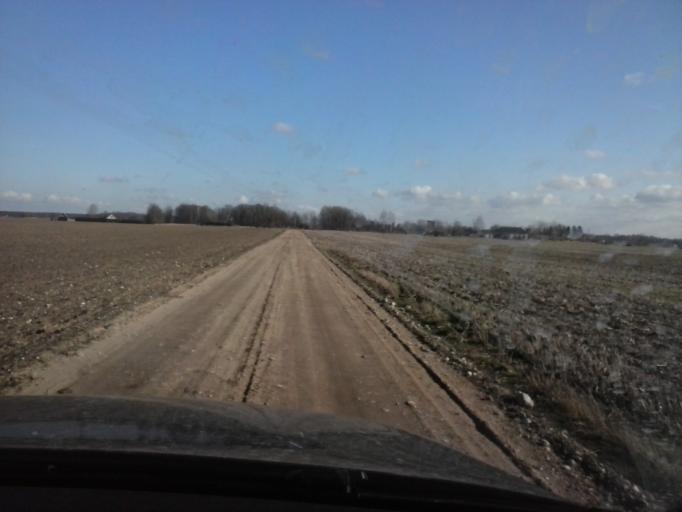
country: EE
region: Tartu
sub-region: Puhja vald
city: Puhja
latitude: 58.2849
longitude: 26.1544
